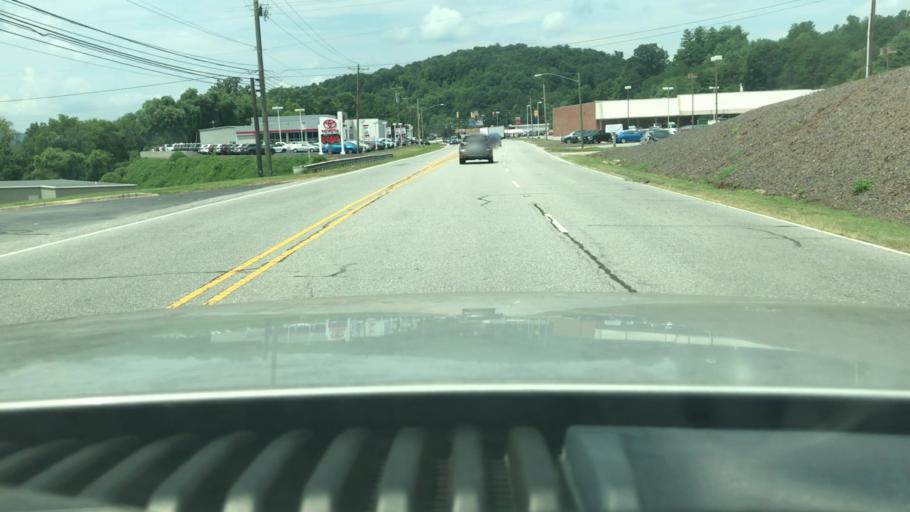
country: US
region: North Carolina
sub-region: Wilkes County
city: Wilkesboro
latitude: 36.1556
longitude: -81.1662
